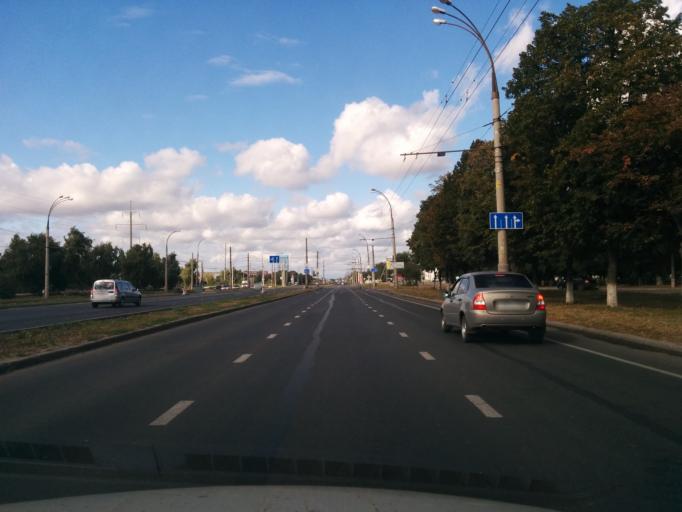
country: RU
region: Samara
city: Tol'yatti
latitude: 53.5377
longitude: 49.2635
